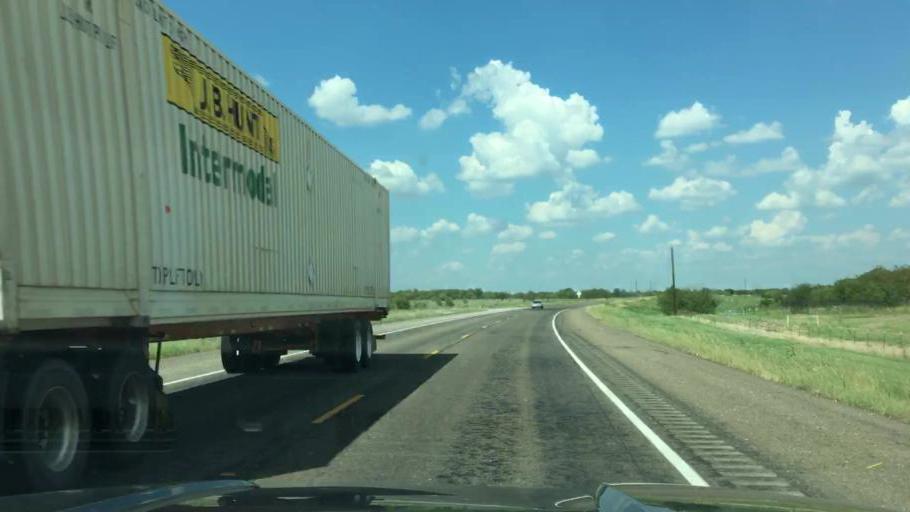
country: US
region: Texas
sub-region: Tarrant County
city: Haslet
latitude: 33.0037
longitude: -97.3423
